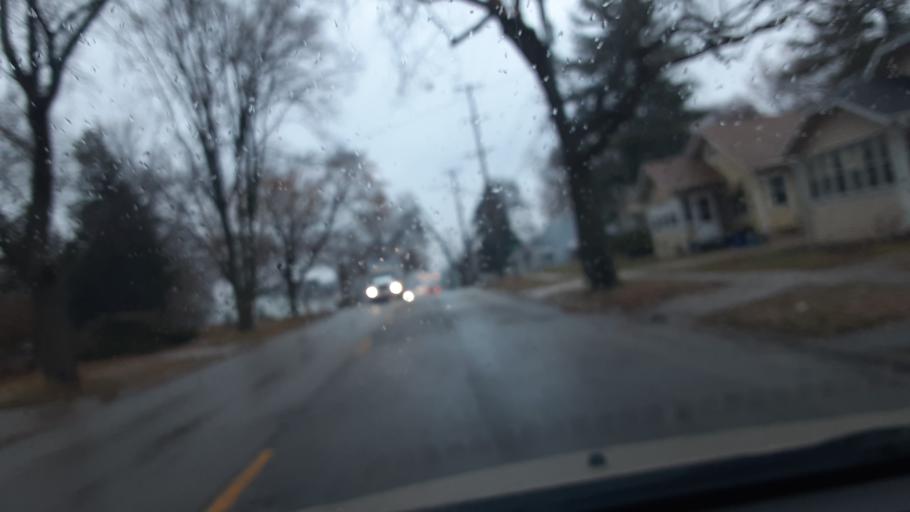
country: US
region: Illinois
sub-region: Winnebago County
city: Rockford
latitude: 42.2858
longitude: -89.1161
